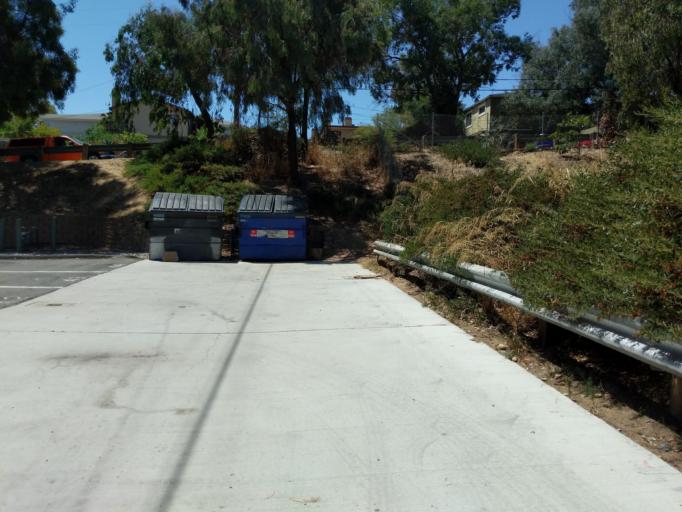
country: US
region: California
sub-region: San Diego County
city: San Diego
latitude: 32.7143
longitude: -117.1314
